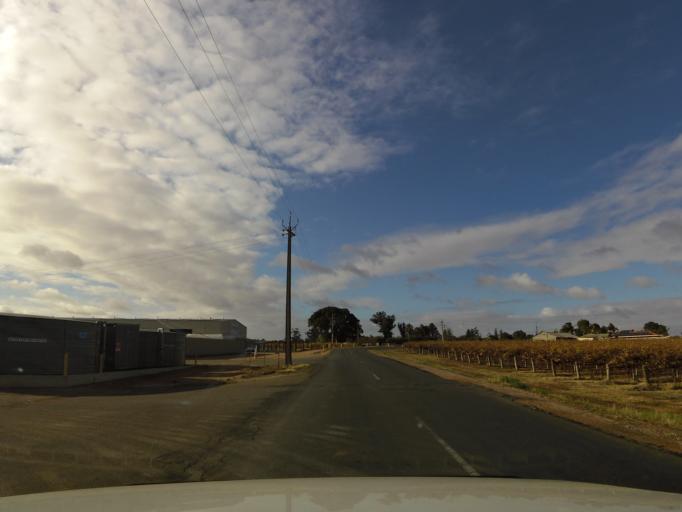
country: AU
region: South Australia
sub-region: Berri and Barmera
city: Berri
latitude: -34.2770
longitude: 140.5780
